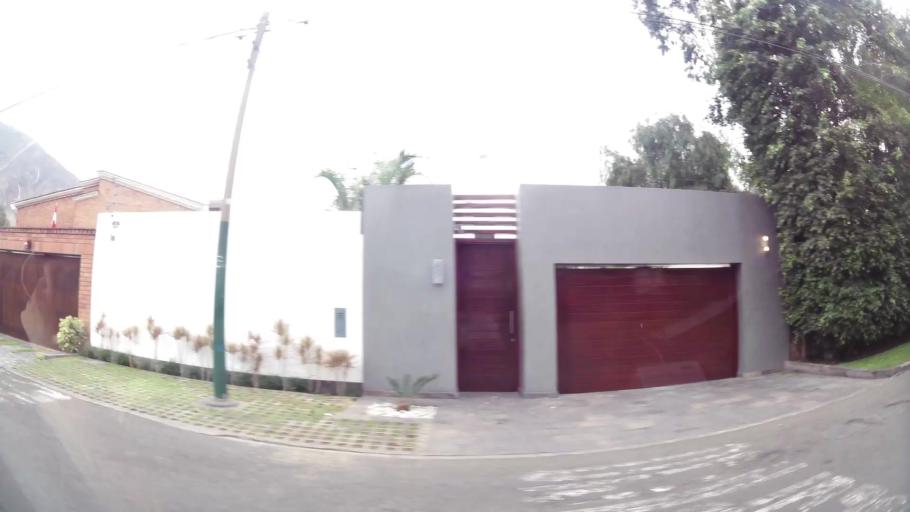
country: PE
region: Lima
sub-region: Lima
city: La Molina
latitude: -12.1086
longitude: -76.9635
